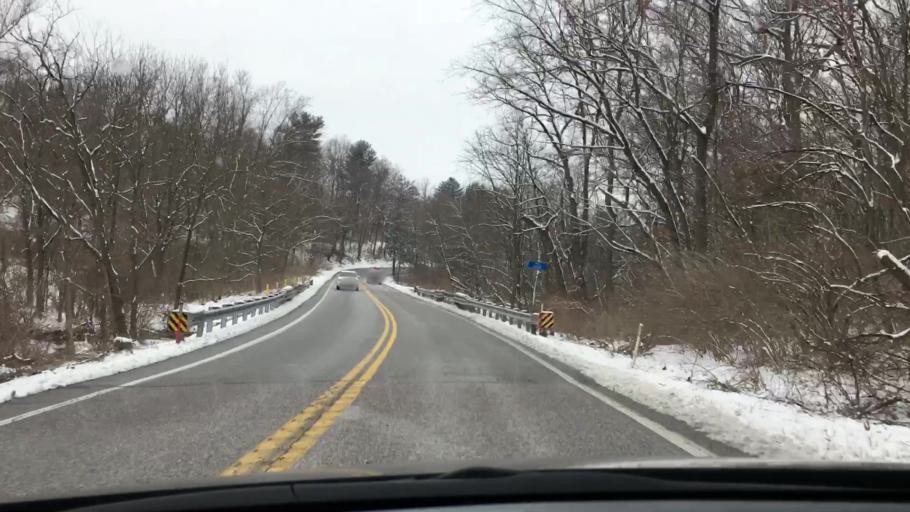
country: US
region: Pennsylvania
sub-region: York County
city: Yoe
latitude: 39.9294
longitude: -76.6527
